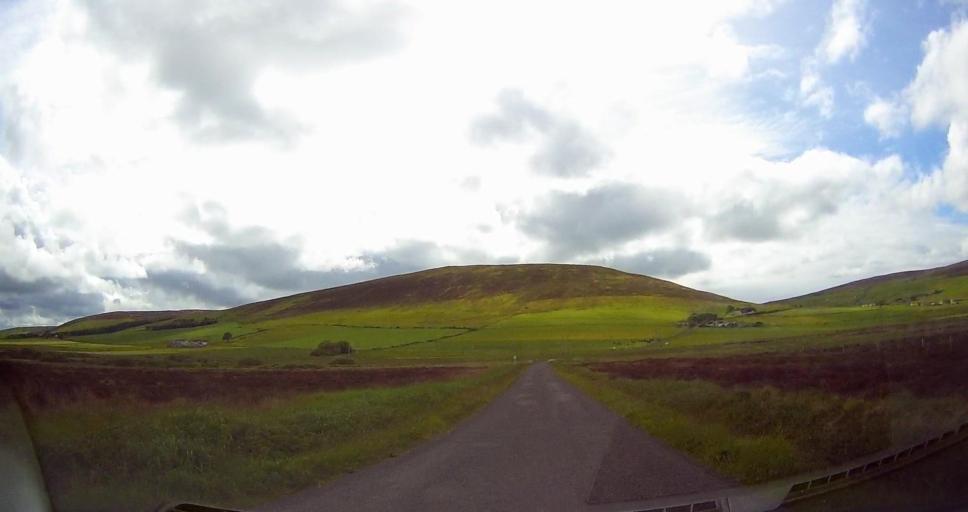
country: GB
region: Scotland
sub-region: Orkney Islands
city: Orkney
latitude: 59.0481
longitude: -3.0871
